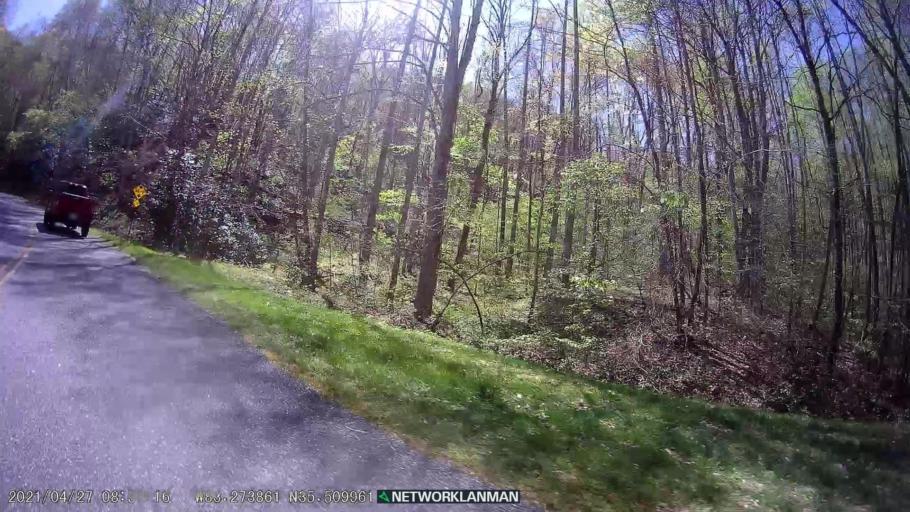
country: US
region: North Carolina
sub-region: Swain County
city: Cherokee
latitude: 35.5098
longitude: -83.2736
